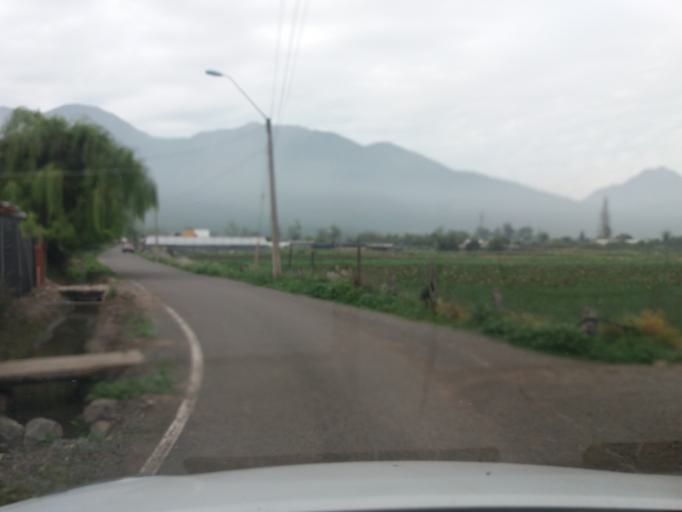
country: CL
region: Valparaiso
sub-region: Provincia de San Felipe
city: Llaillay
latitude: -32.8425
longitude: -71.0655
